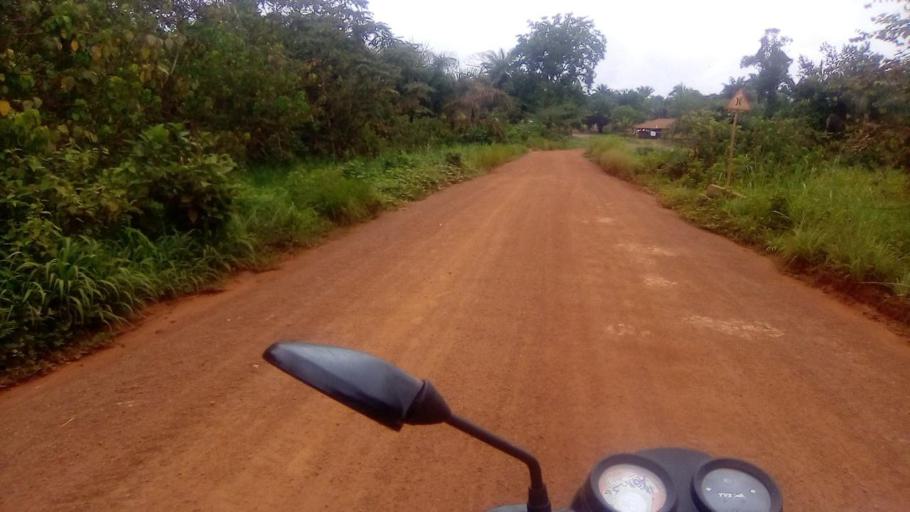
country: SL
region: Southern Province
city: Tongole
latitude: 7.4378
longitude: -11.8629
